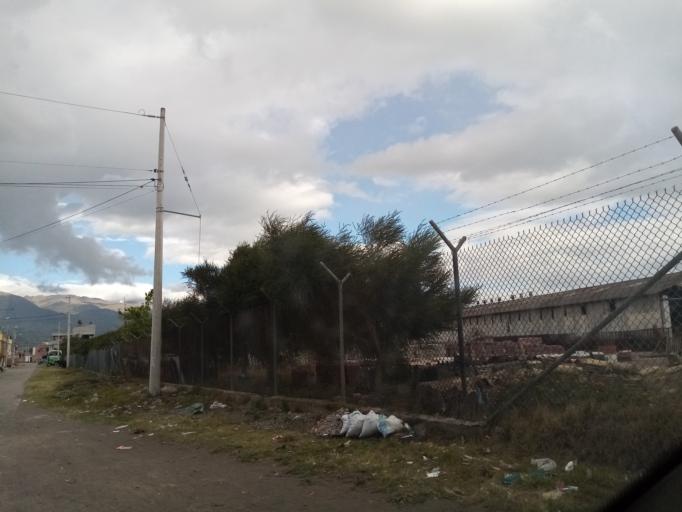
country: EC
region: Chimborazo
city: Riobamba
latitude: -1.6893
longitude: -78.6295
